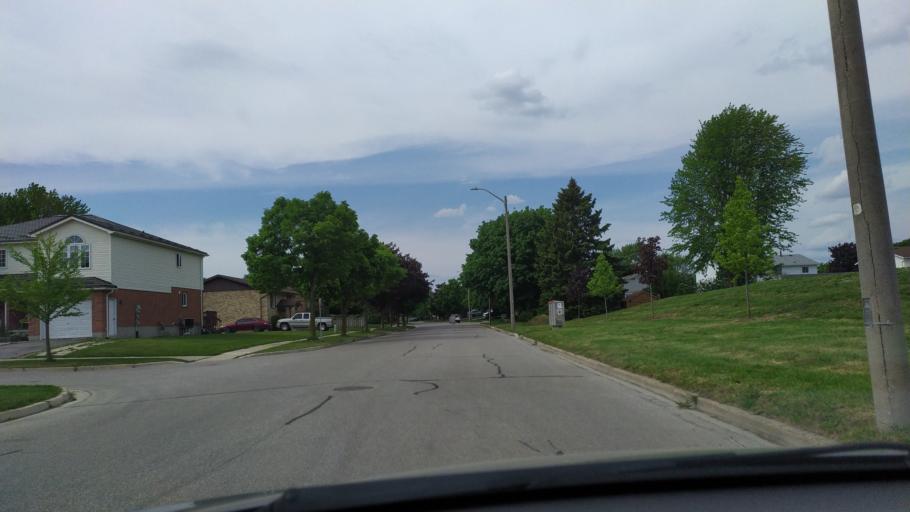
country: CA
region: Ontario
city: Stratford
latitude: 43.3541
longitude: -80.9849
